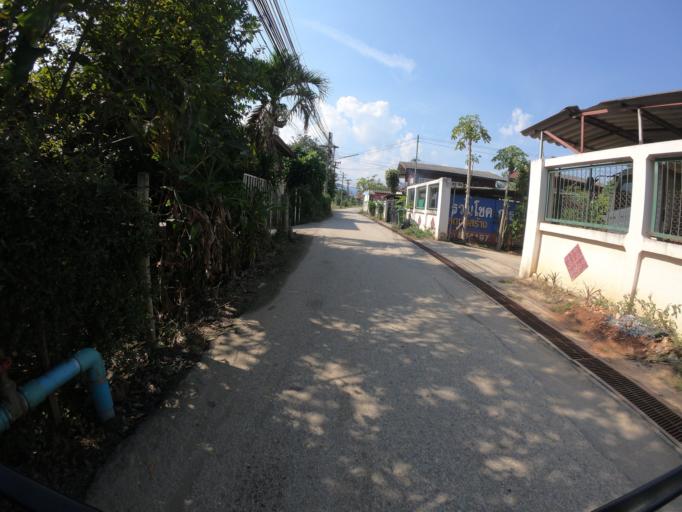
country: TH
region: Chiang Mai
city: San Sai
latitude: 18.8519
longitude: 98.9996
